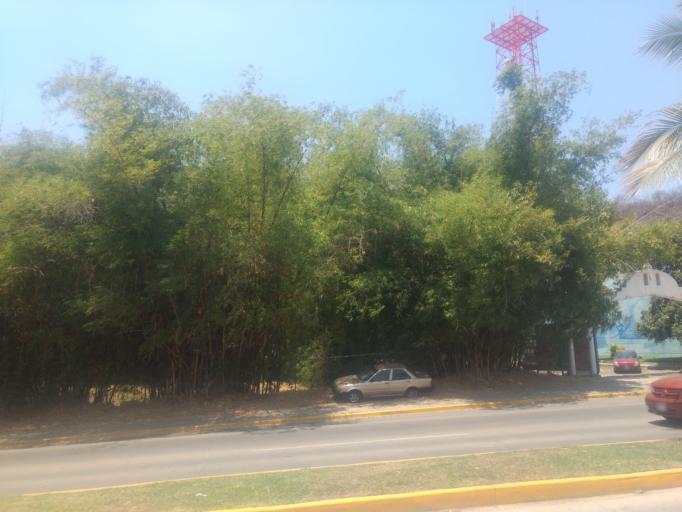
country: MX
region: Colima
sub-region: Manzanillo
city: Manzanillo
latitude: 19.1151
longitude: -104.3469
